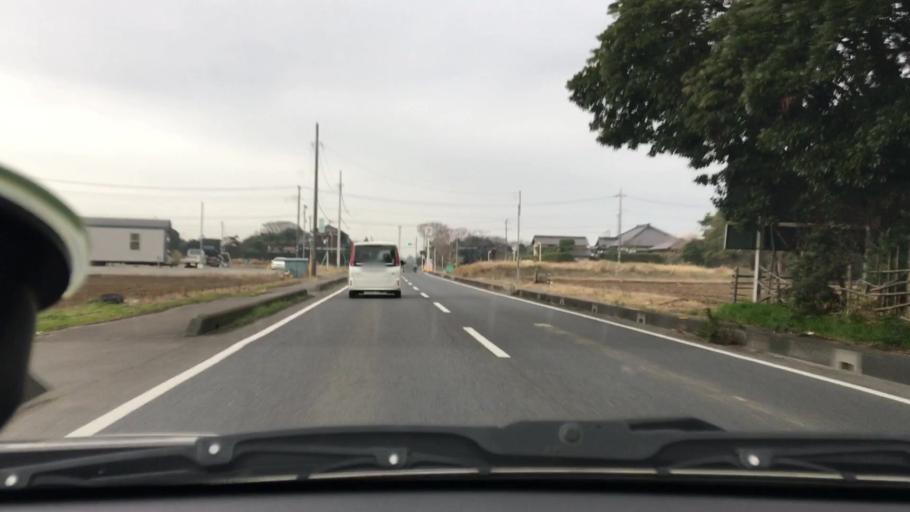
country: JP
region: Chiba
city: Omigawa
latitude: 35.8727
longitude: 140.6408
